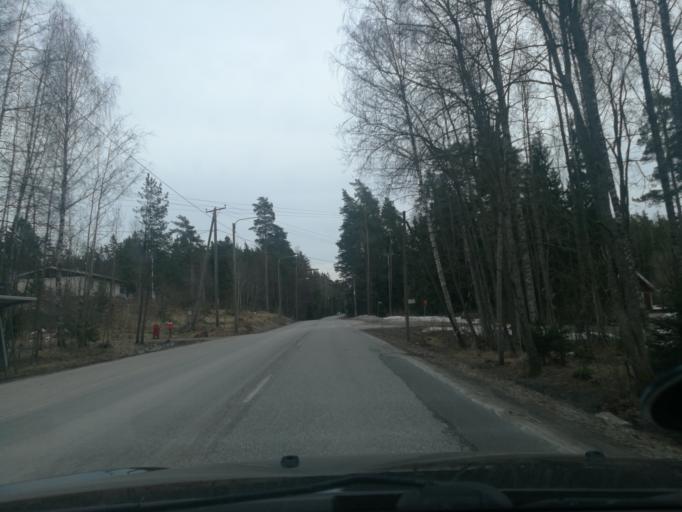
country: FI
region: Uusimaa
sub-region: Helsinki
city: Nickby
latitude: 60.2766
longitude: 25.3824
